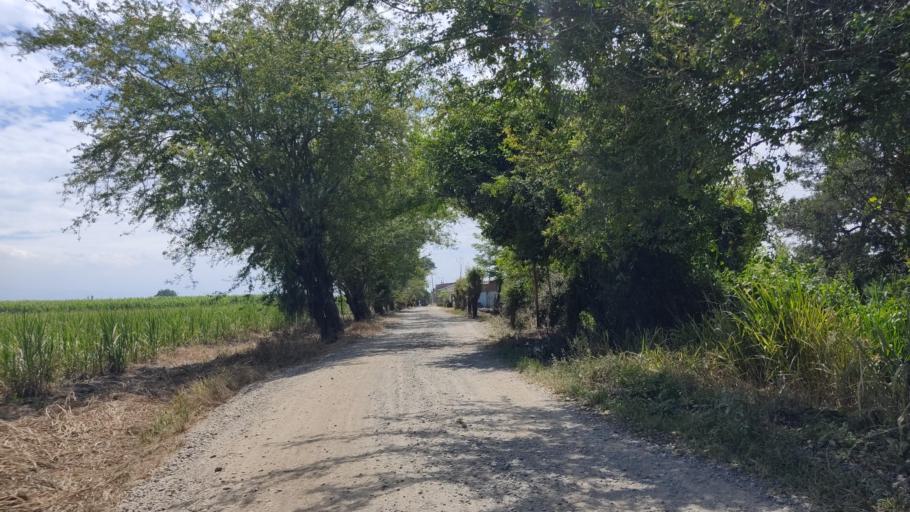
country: CO
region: Valle del Cauca
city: Jamundi
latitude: 3.1598
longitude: -76.5124
